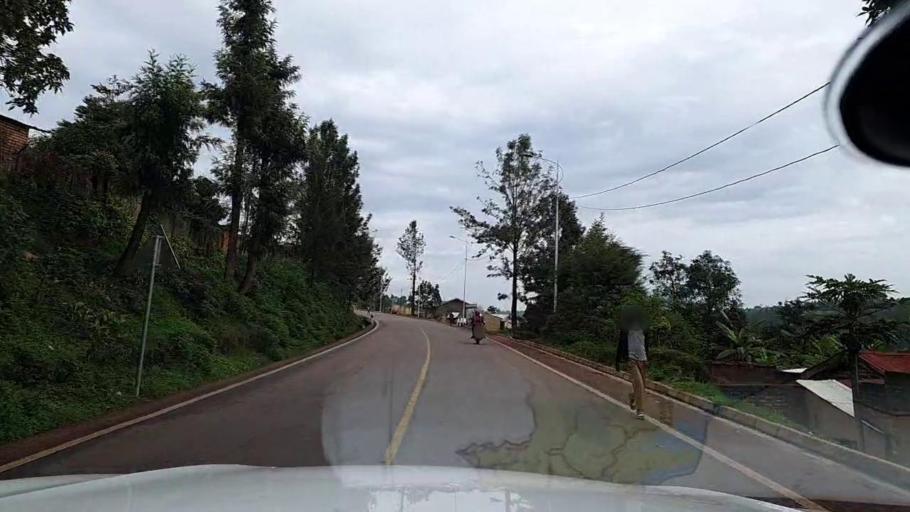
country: RW
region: Southern Province
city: Butare
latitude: -2.5820
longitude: 29.7363
